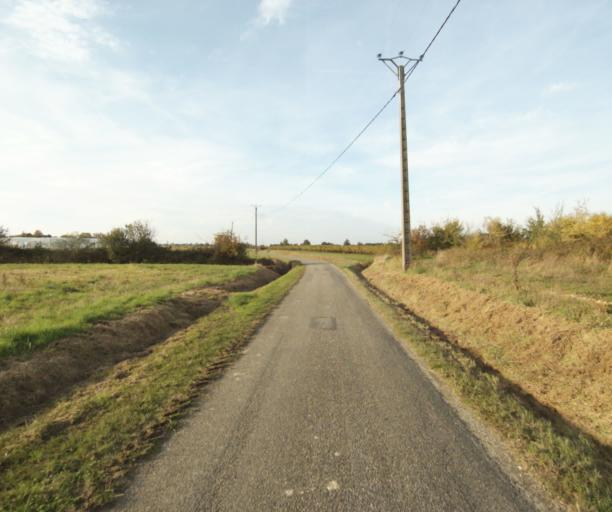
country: FR
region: Midi-Pyrenees
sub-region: Departement du Tarn-et-Garonne
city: Campsas
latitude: 43.8794
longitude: 1.3485
